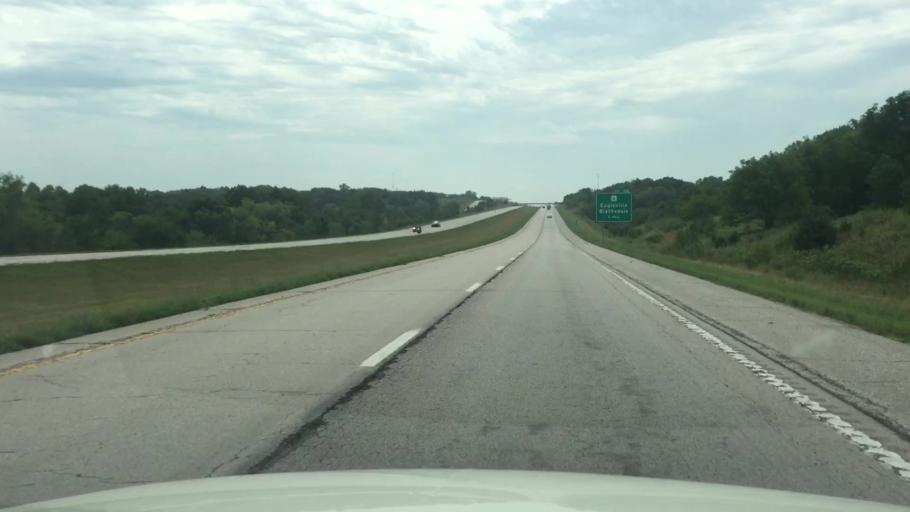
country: US
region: Iowa
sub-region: Decatur County
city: Lamoni
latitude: 40.4838
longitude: -93.9723
